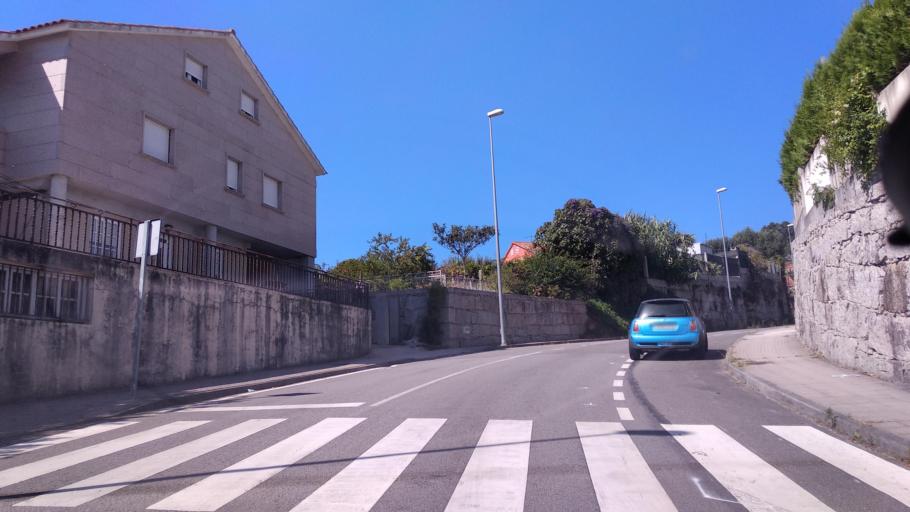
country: ES
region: Galicia
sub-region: Provincia de Pontevedra
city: Moana
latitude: 42.2766
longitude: -8.7686
